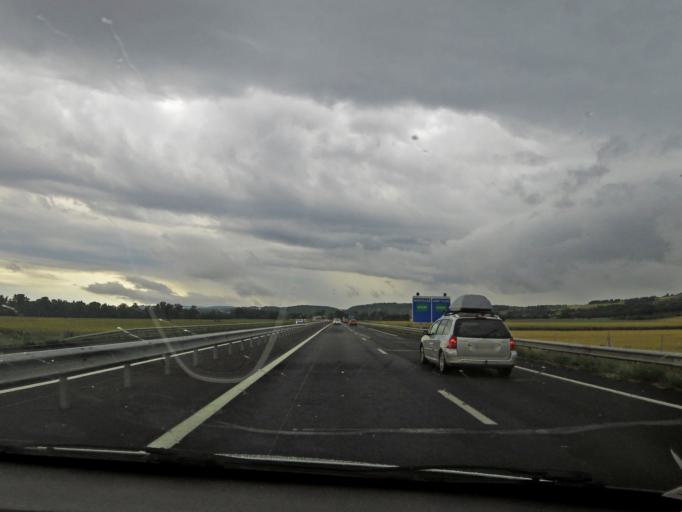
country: FR
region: Auvergne
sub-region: Departement de la Haute-Loire
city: Lempdes-sur-Allagnon
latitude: 45.4036
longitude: 3.2739
